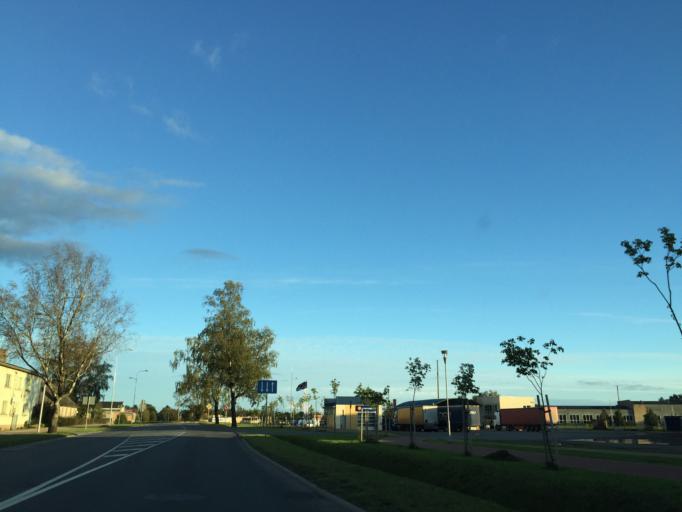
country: LV
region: Saldus Rajons
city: Saldus
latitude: 56.6838
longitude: 22.4706
